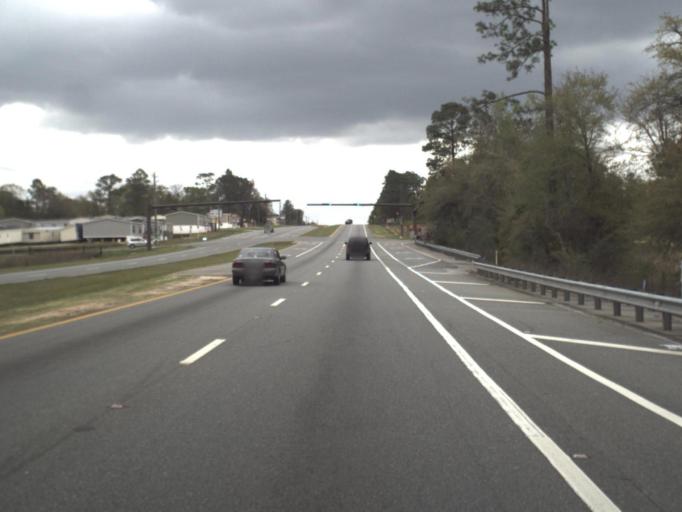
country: US
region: Florida
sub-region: Okaloosa County
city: Crestview
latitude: 30.6988
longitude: -86.5713
